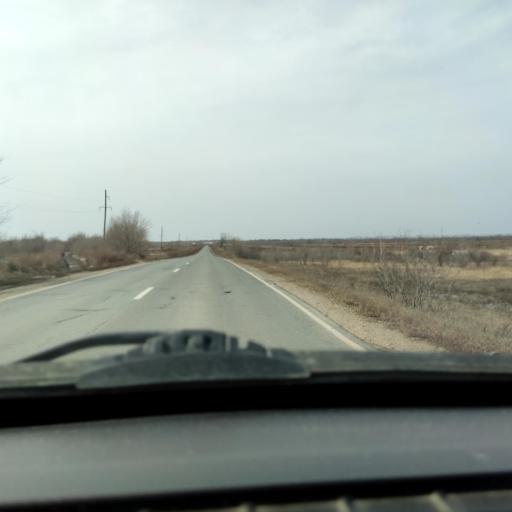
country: RU
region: Samara
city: Smyshlyayevka
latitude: 53.1549
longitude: 50.4495
